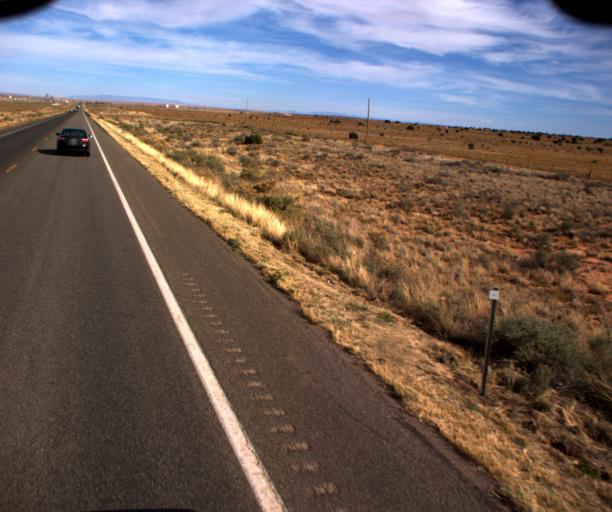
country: US
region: Arizona
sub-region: Navajo County
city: Kayenta
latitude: 36.7016
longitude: -110.2871
